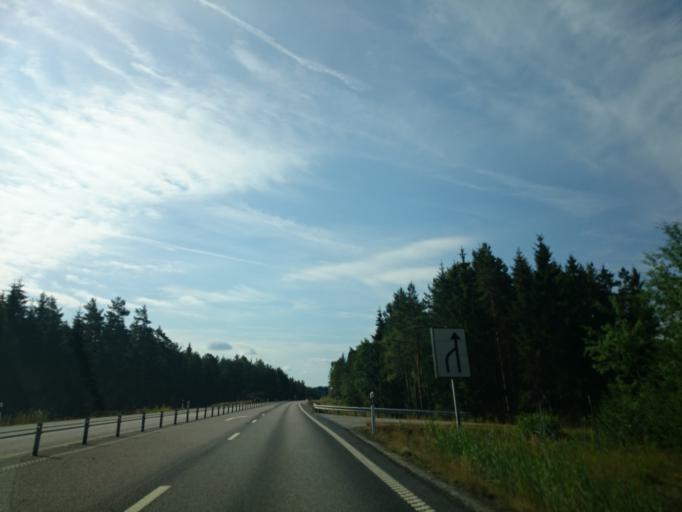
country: SE
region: OEstergoetland
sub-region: Valdemarsviks Kommun
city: Valdemarsvik
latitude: 58.2366
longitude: 16.5477
